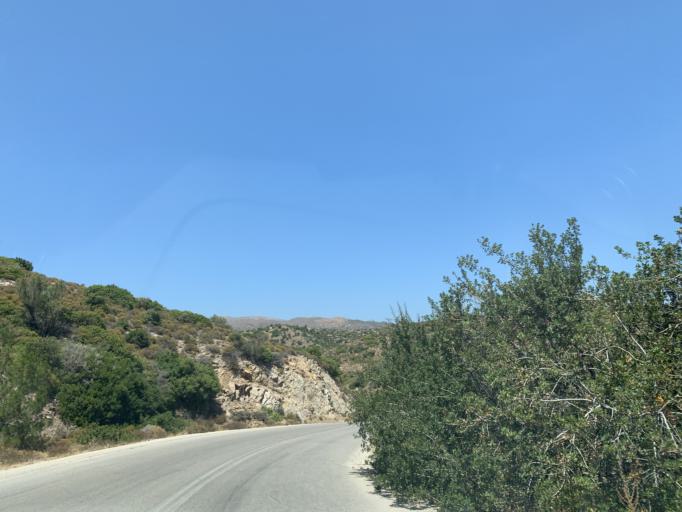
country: GR
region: North Aegean
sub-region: Chios
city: Vrontados
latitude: 38.4692
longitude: 25.9599
